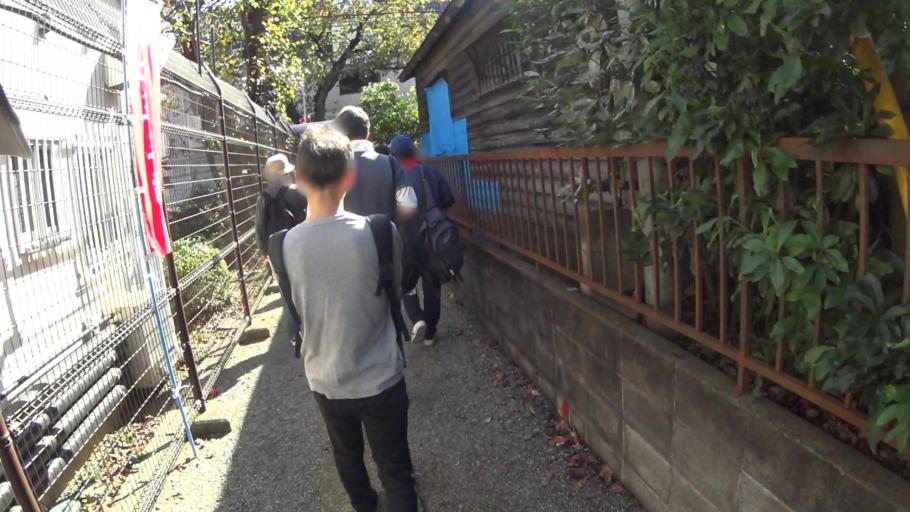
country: JP
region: Tokyo
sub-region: Machida-shi
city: Machida
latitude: 35.5470
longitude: 139.4504
